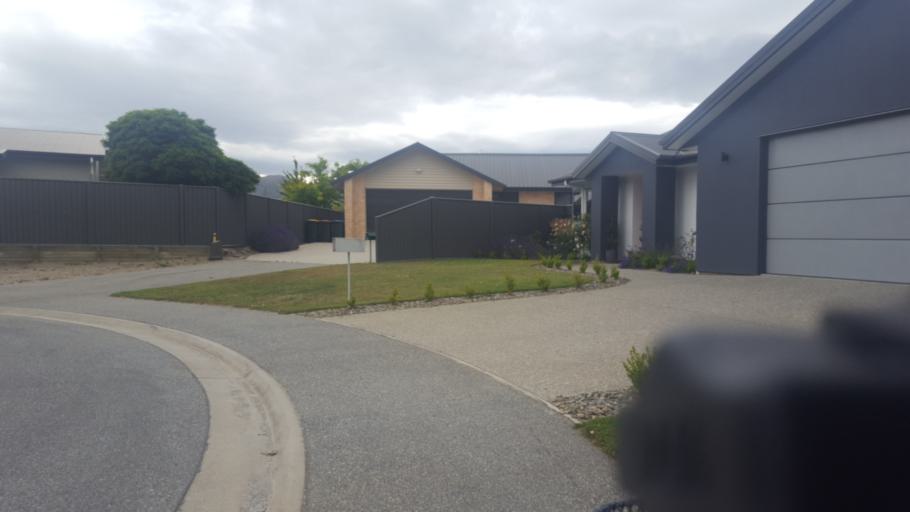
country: NZ
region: Otago
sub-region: Queenstown-Lakes District
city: Wanaka
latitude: -45.0469
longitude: 169.1877
